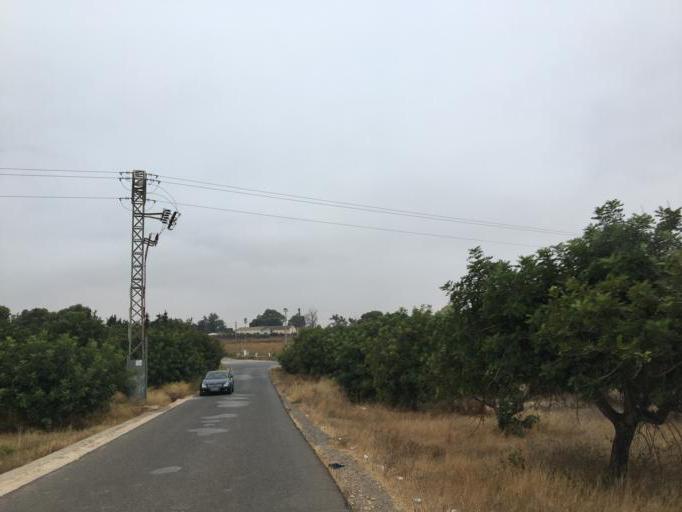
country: ES
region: Murcia
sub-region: Murcia
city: Cartagena
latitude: 37.6619
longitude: -1.0077
